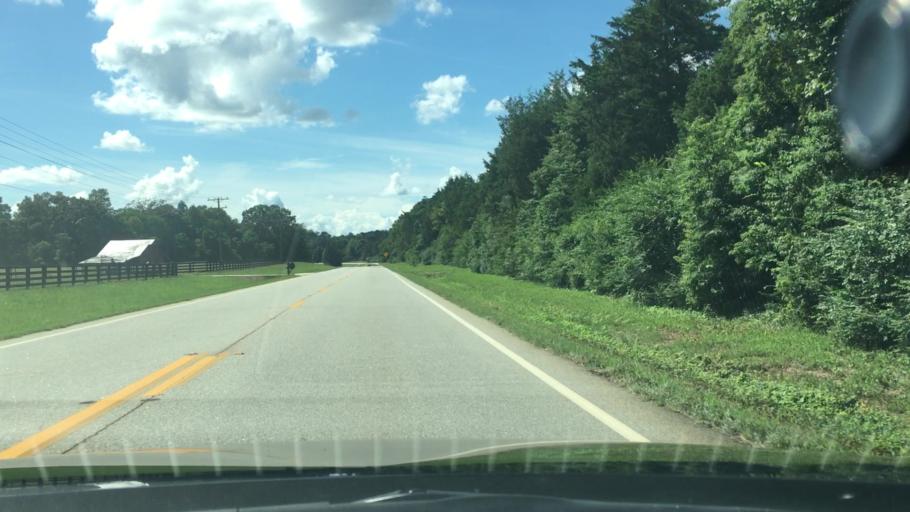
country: US
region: Georgia
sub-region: Jasper County
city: Monticello
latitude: 33.3136
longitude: -83.7487
